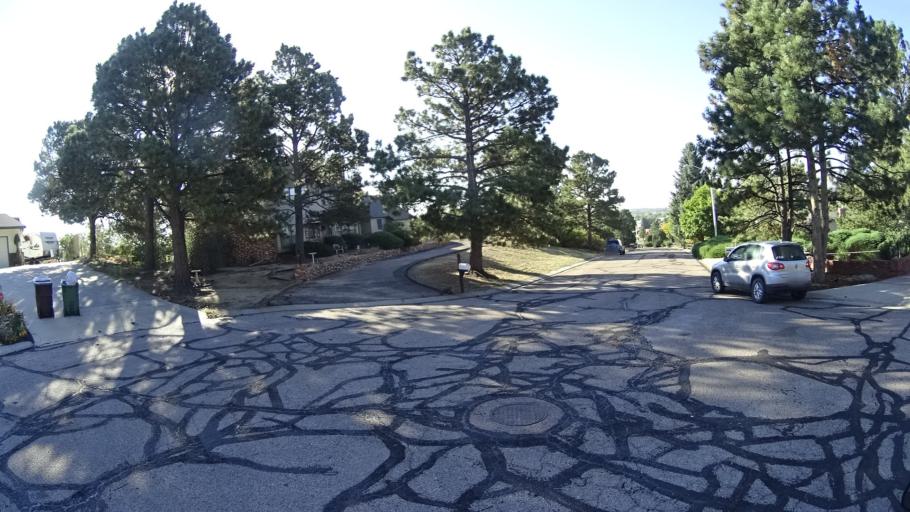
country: US
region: Colorado
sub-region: El Paso County
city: Cimarron Hills
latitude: 38.9095
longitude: -104.7580
